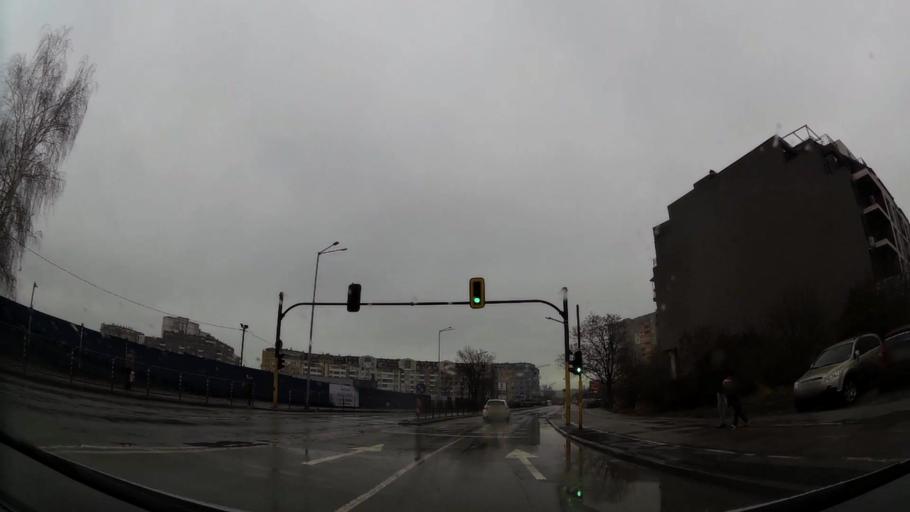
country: BG
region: Sofia-Capital
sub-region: Stolichna Obshtina
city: Sofia
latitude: 42.6463
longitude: 23.3772
